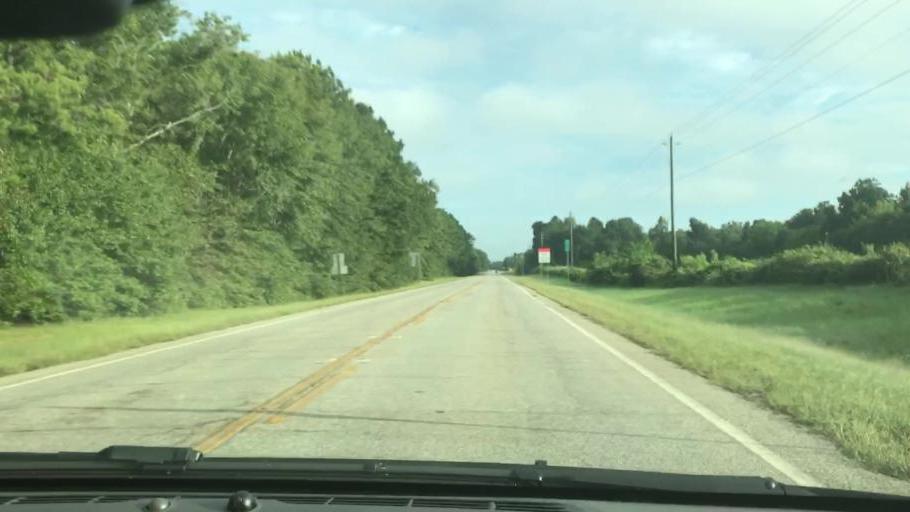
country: US
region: Georgia
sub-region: Clay County
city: Fort Gaines
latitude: 31.7251
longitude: -85.0450
